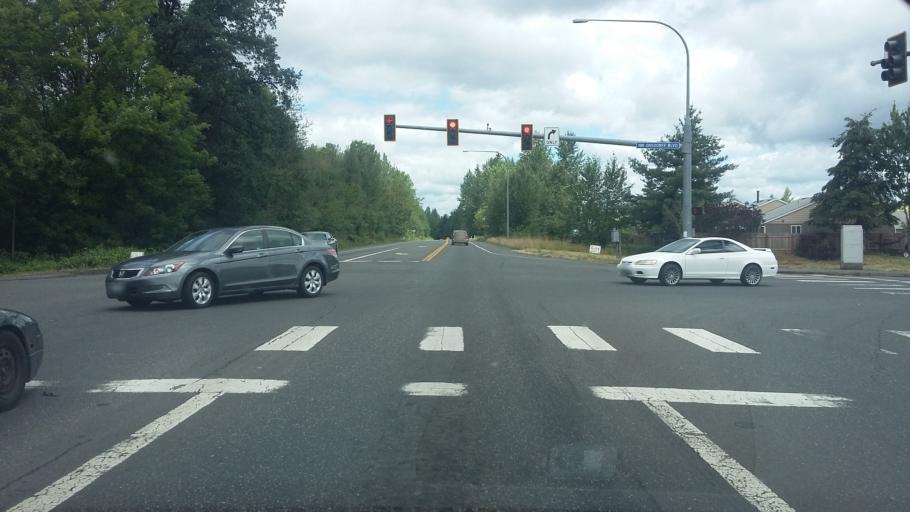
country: US
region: Washington
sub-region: Clark County
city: Battle Ground
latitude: 45.7914
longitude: -122.5474
